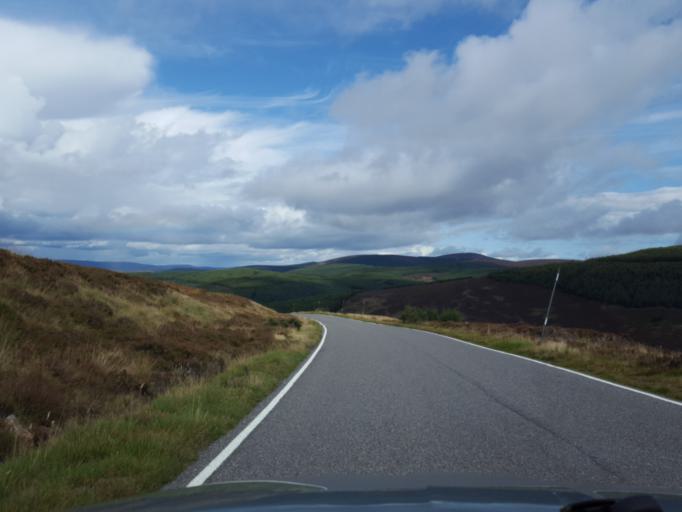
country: GB
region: Scotland
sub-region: Aberdeenshire
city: Laurencekirk
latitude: 56.9316
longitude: -2.5718
